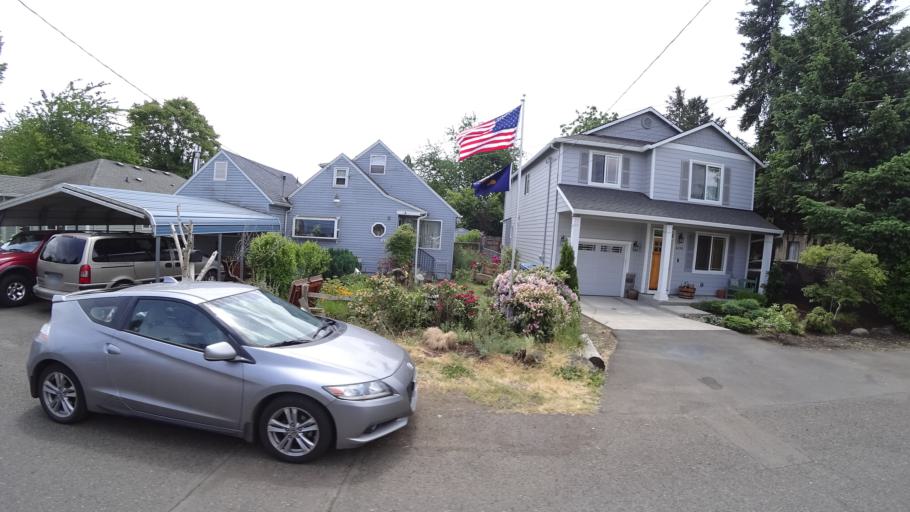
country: US
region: Oregon
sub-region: Multnomah County
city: Lents
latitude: 45.4700
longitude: -122.6008
